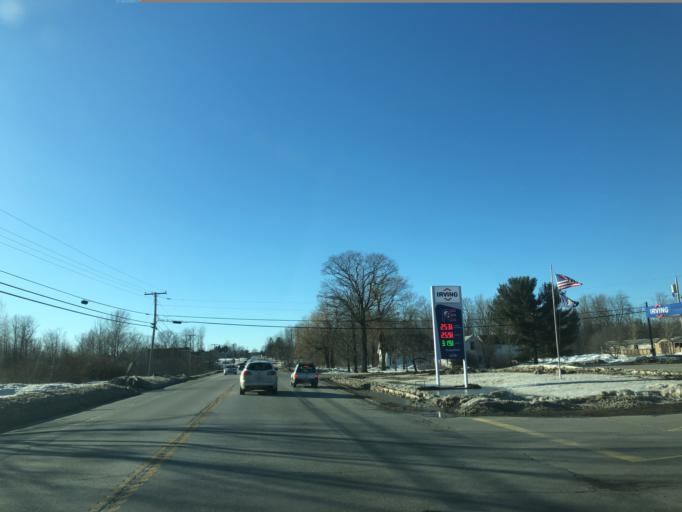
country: US
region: Maine
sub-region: Penobscot County
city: Kenduskeag
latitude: 44.9855
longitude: -69.0066
